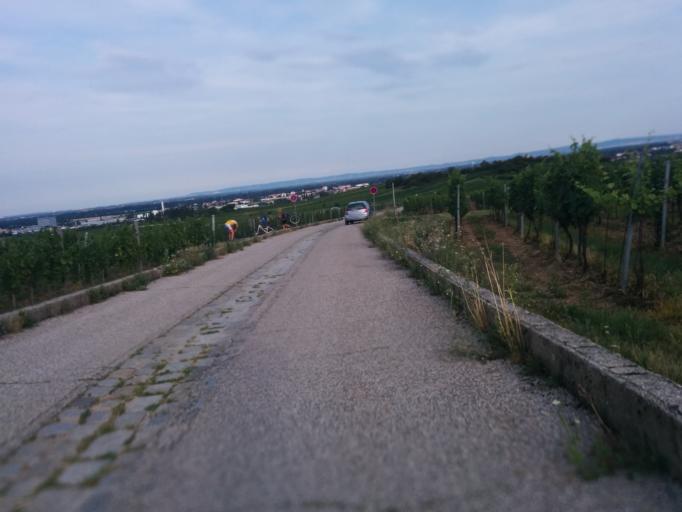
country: AT
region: Lower Austria
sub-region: Politischer Bezirk Modling
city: Gumpoldskirchen
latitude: 48.0353
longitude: 16.2636
